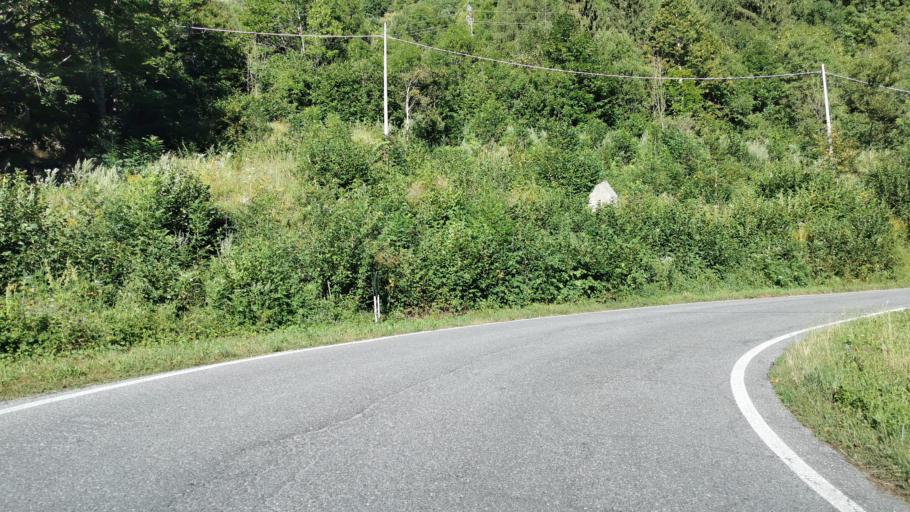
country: IT
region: Piedmont
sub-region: Provincia di Cuneo
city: Entracque
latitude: 44.2369
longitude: 7.3170
